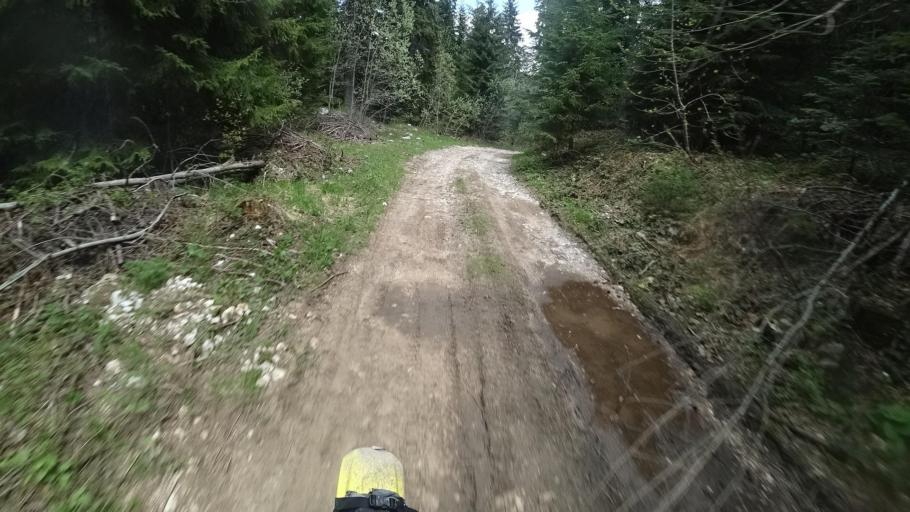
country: BA
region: Republika Srpska
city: Sipovo
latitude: 44.0841
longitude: 17.0958
